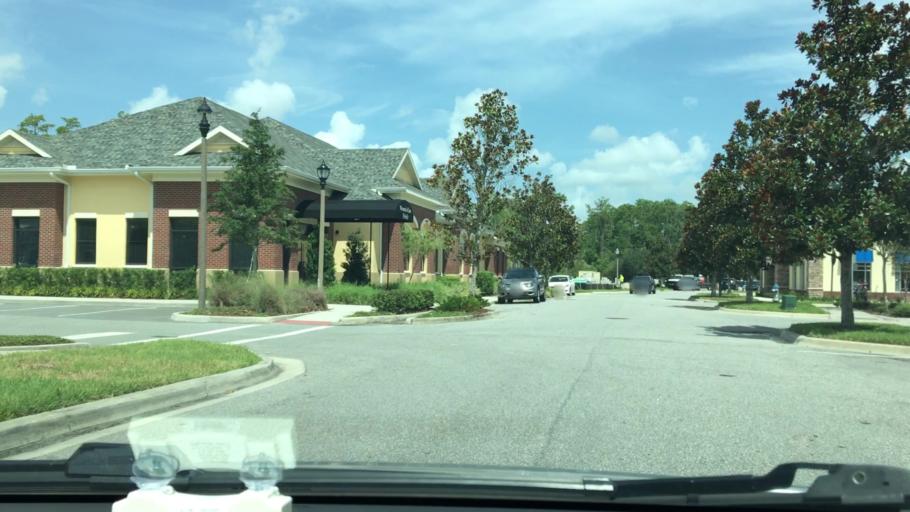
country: US
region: Florida
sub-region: Orange County
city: Conway
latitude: 28.4255
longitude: -81.2539
